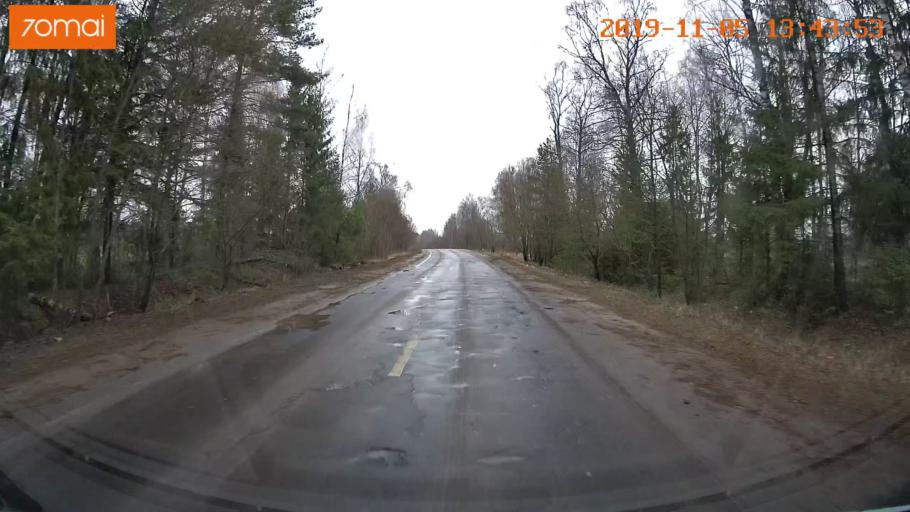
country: RU
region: Ivanovo
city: Shuya
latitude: 56.9768
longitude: 41.4065
